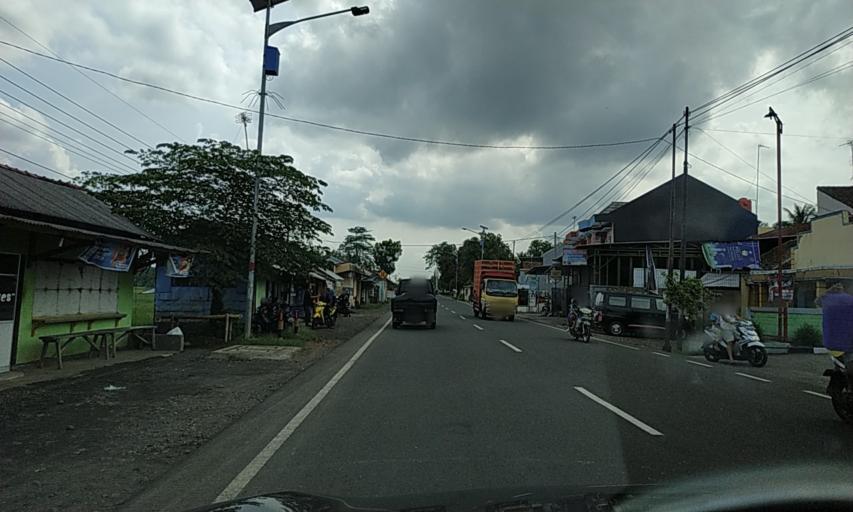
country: ID
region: Central Java
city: Sogati
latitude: -7.3337
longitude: 108.6753
